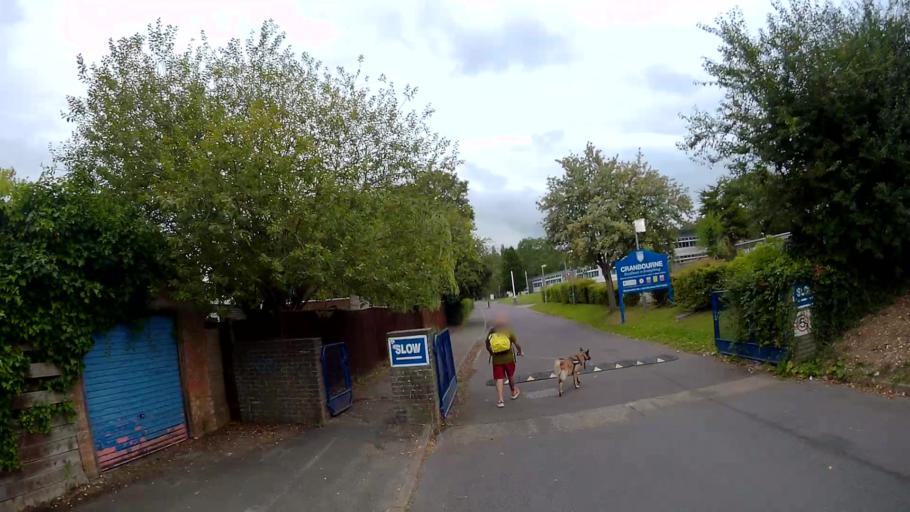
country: GB
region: England
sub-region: Hampshire
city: Basingstoke
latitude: 51.2563
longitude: -1.0984
